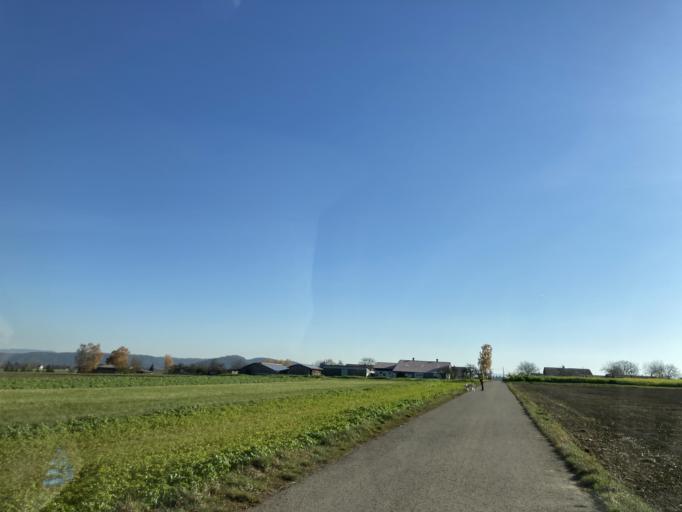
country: DE
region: Baden-Wuerttemberg
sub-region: Tuebingen Region
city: Rottenburg
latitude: 48.4776
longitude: 8.8880
